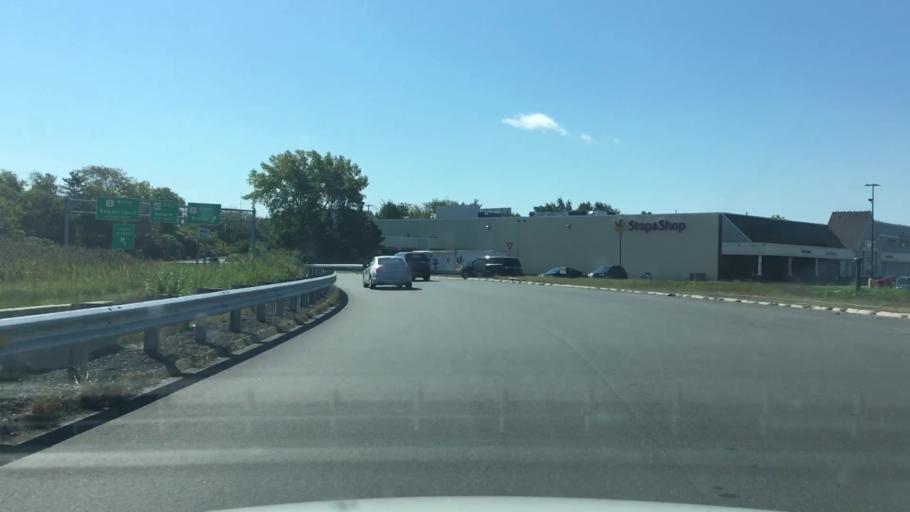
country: US
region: Massachusetts
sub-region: Suffolk County
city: Revere
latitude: 42.4305
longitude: -71.0192
